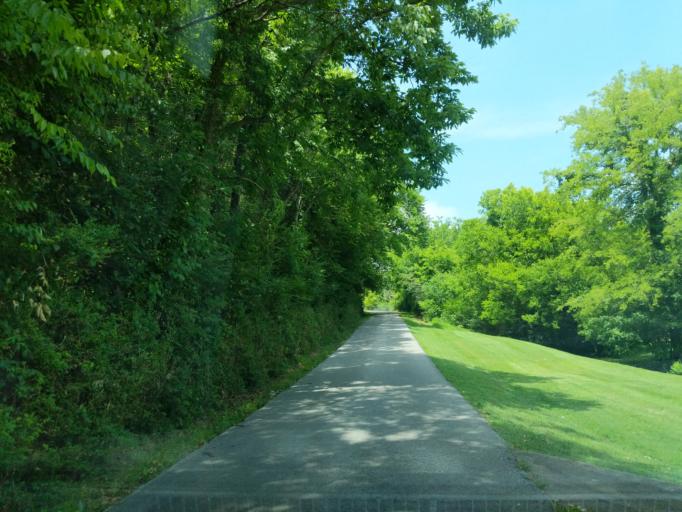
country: US
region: Tennessee
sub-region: Davidson County
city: Goodlettsville
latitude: 36.3127
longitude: -86.7320
